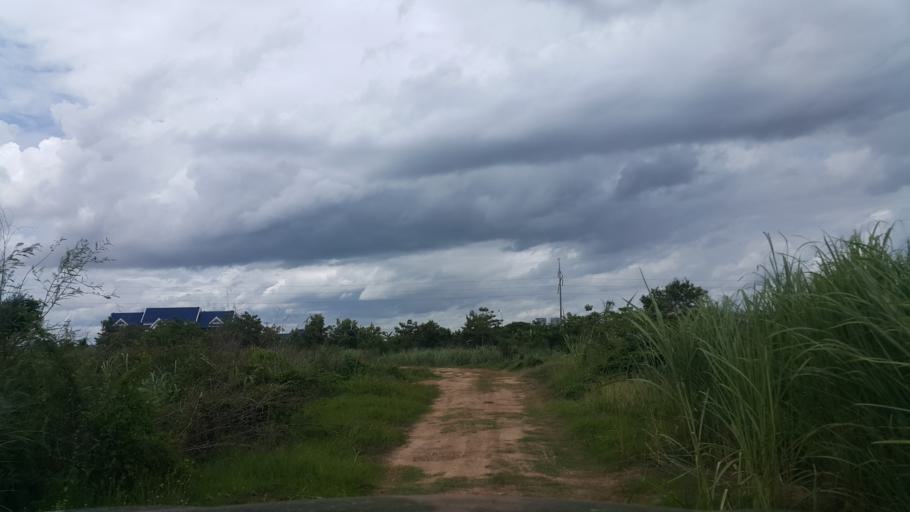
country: TH
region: Sukhothai
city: Sukhothai
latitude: 17.0323
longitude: 99.7994
